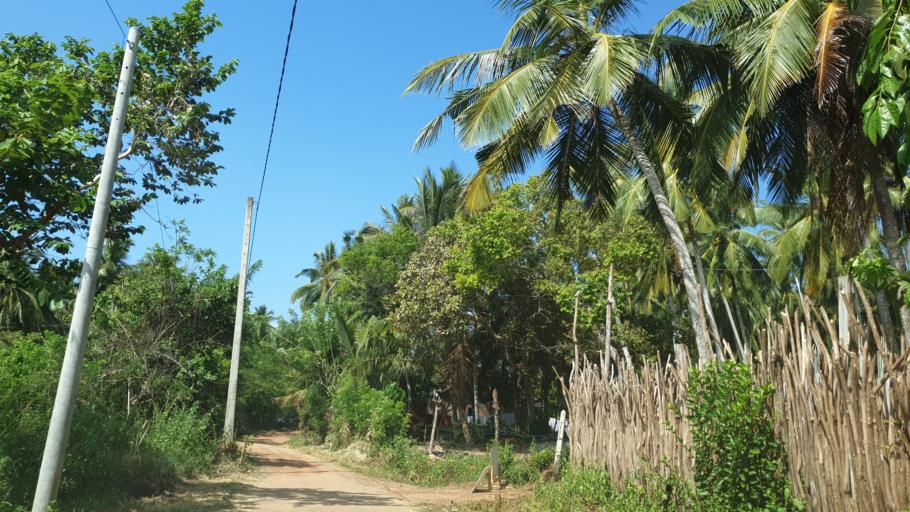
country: LK
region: Southern
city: Tangalla
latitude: 5.9611
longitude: 80.7117
